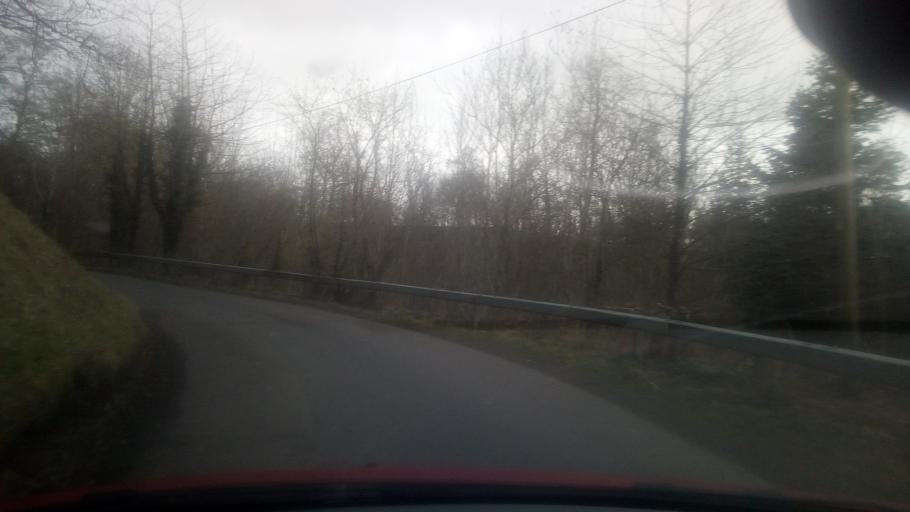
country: GB
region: Scotland
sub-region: The Scottish Borders
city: Jedburgh
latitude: 55.4734
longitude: -2.5384
